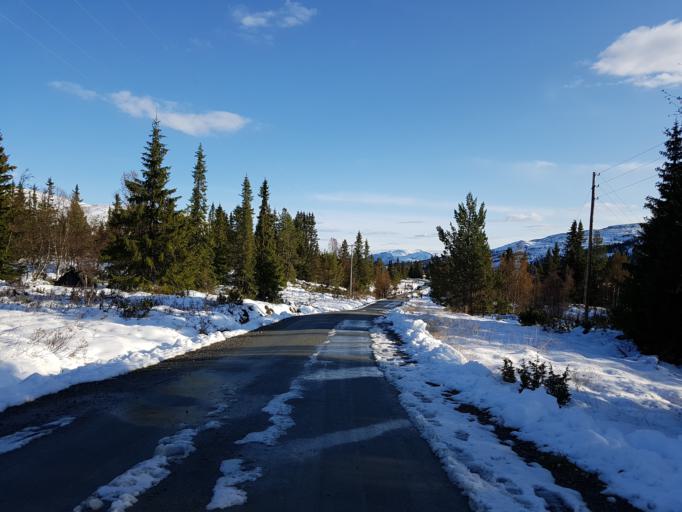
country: NO
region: Oppland
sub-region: Sel
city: Otta
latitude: 61.8155
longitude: 9.6794
